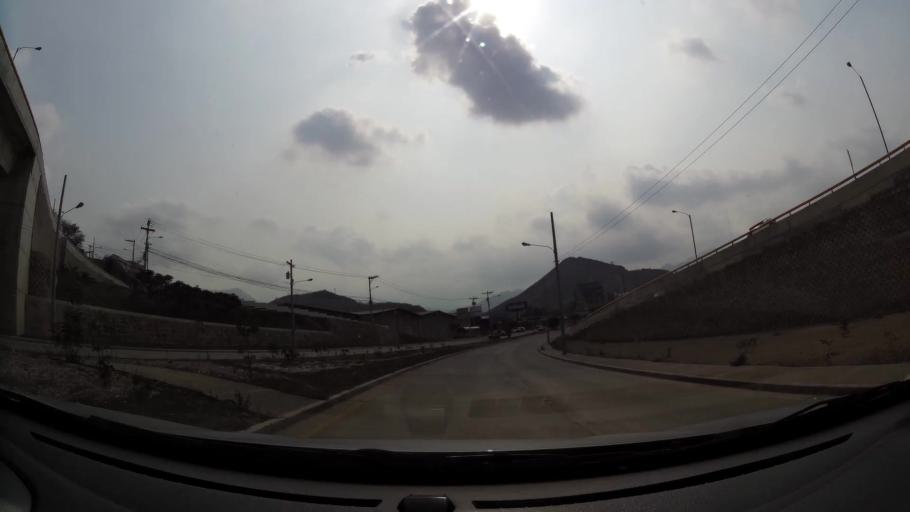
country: HN
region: Francisco Morazan
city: Tegucigalpa
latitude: 14.1084
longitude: -87.1691
